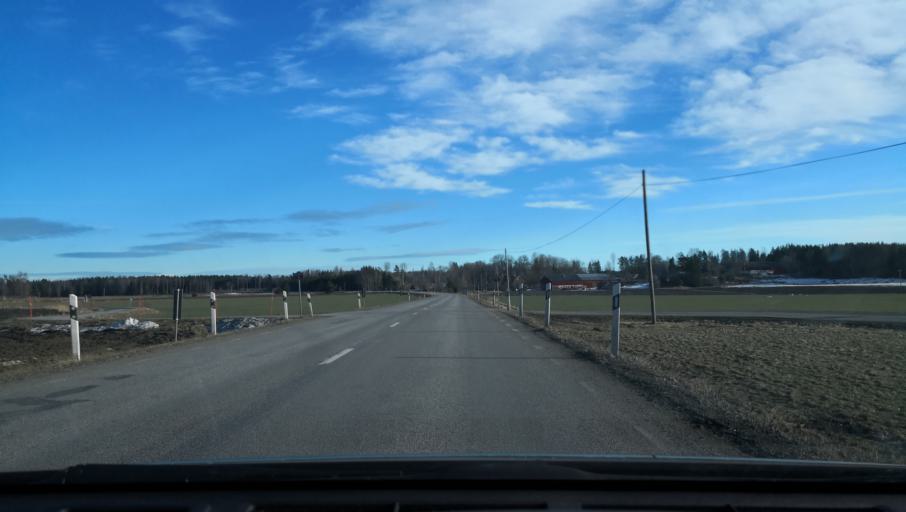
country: SE
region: Uppsala
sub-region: Osthammars Kommun
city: Osterbybruk
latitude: 60.1651
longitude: 17.9772
